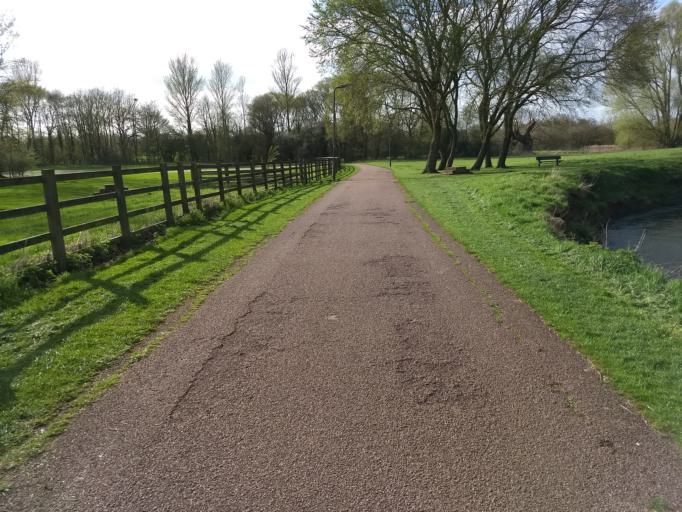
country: GB
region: England
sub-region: Milton Keynes
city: Simpson
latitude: 52.0235
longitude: -0.7140
